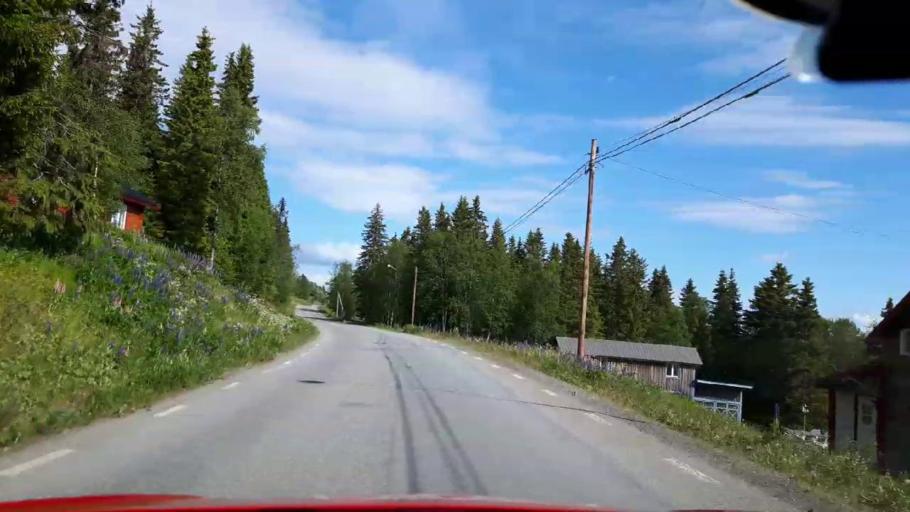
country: SE
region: Jaemtland
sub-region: Krokoms Kommun
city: Valla
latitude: 63.7693
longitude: 14.0570
